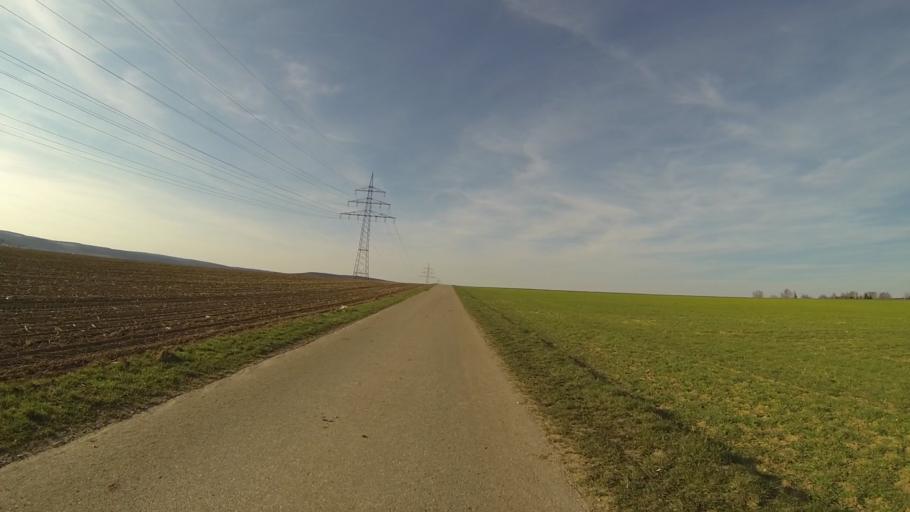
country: DE
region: Baden-Wuerttemberg
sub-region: Regierungsbezirk Stuttgart
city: Herbrechtingen
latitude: 48.6123
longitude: 10.1944
